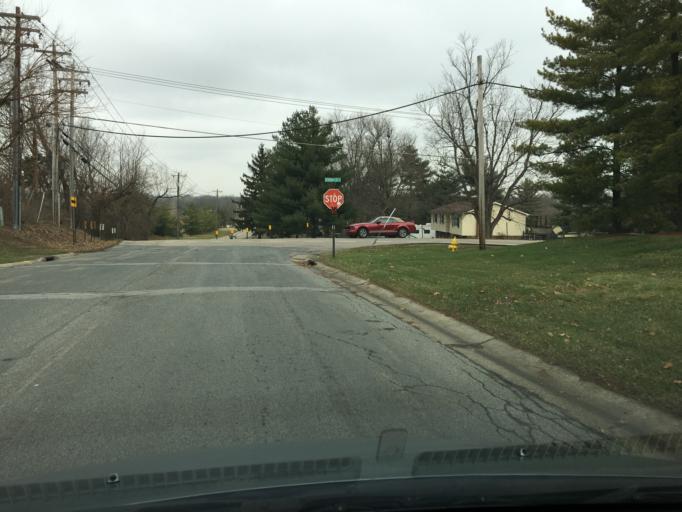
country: US
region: Ohio
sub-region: Hamilton County
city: Sharonville
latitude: 39.3123
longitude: -84.3996
